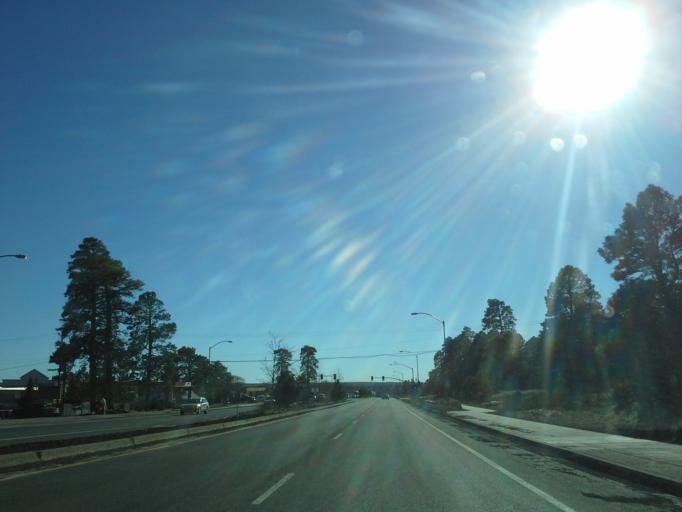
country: US
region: Arizona
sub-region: Coconino County
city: Flagstaff
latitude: 35.2348
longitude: -111.5750
